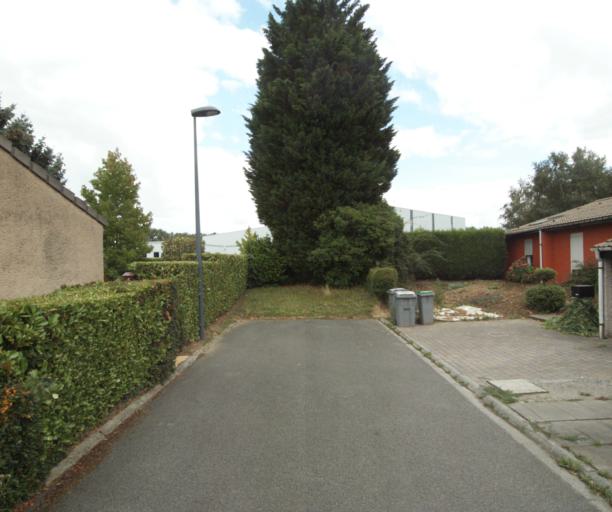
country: FR
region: Nord-Pas-de-Calais
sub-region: Departement du Nord
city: Villeneuve-d'Ascq
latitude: 50.6124
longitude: 3.1514
